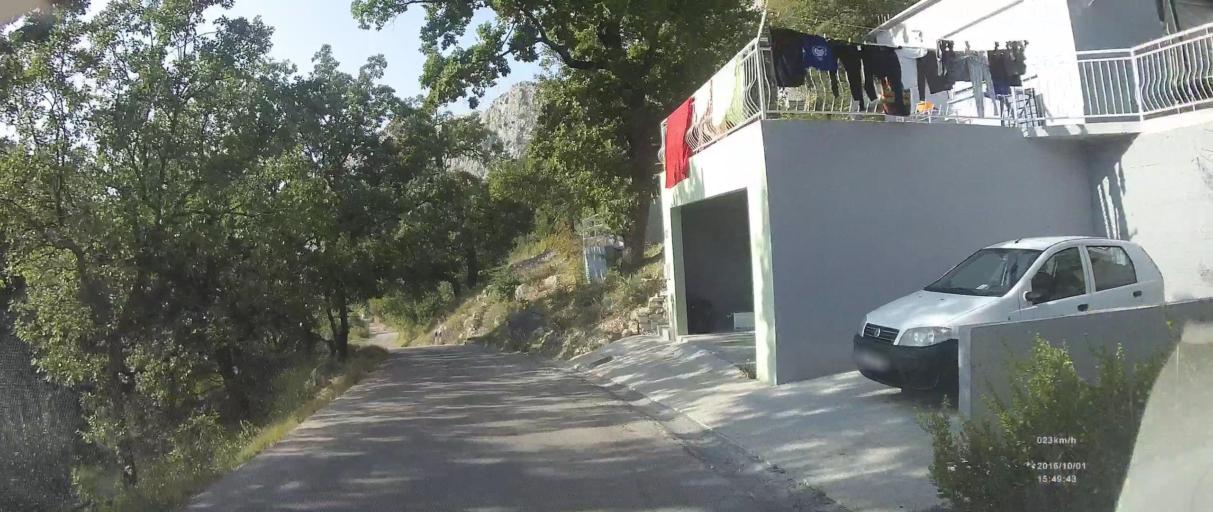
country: HR
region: Splitsko-Dalmatinska
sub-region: Grad Omis
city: Omis
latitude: 43.4406
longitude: 16.7061
